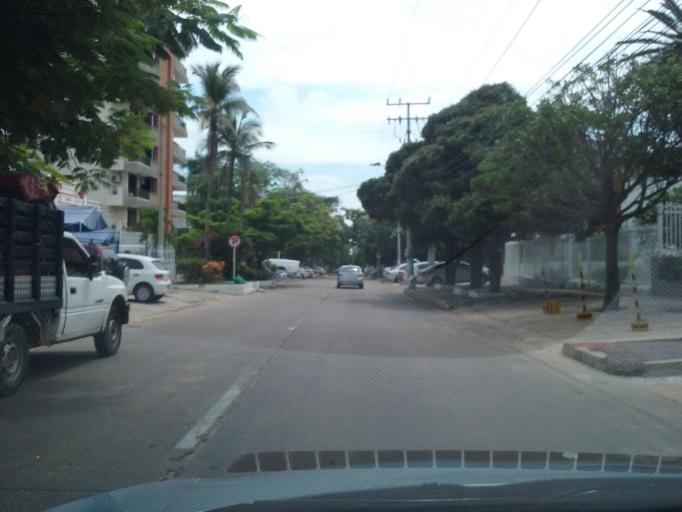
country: CO
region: Atlantico
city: Barranquilla
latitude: 11.0034
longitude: -74.8014
